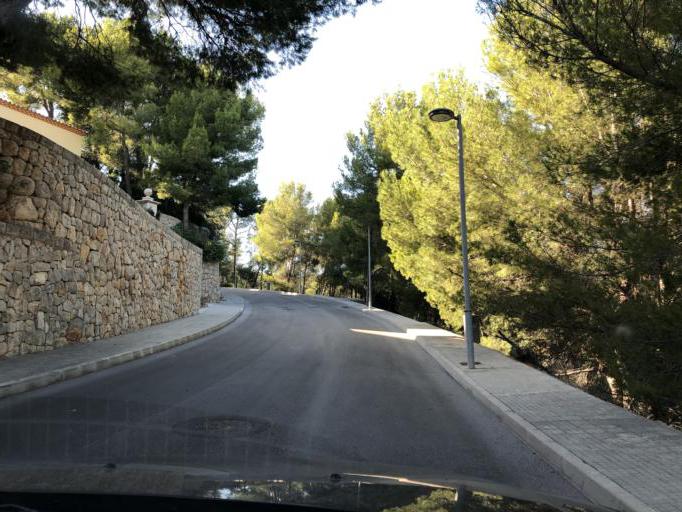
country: ES
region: Balearic Islands
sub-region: Illes Balears
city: Camp de Mar
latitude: 39.5381
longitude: 2.4119
